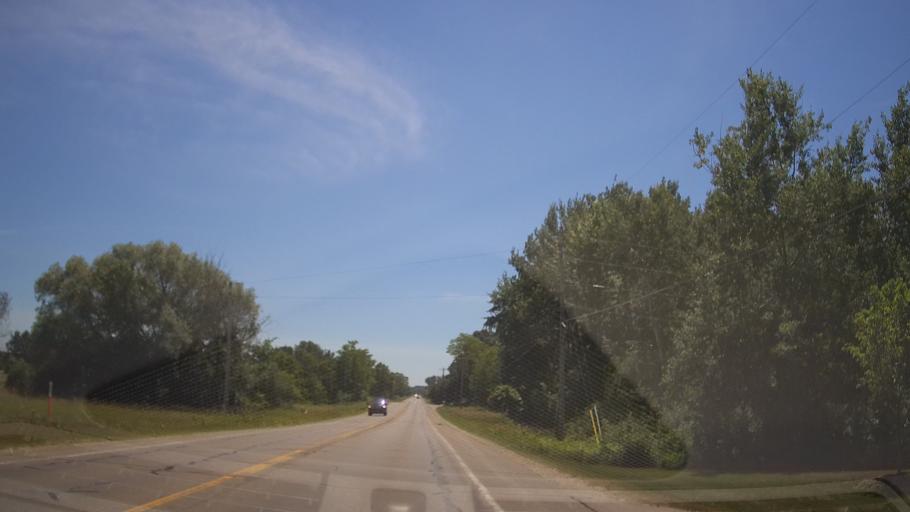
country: US
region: Michigan
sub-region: Grand Traverse County
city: Traverse City
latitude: 44.6811
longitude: -85.6897
